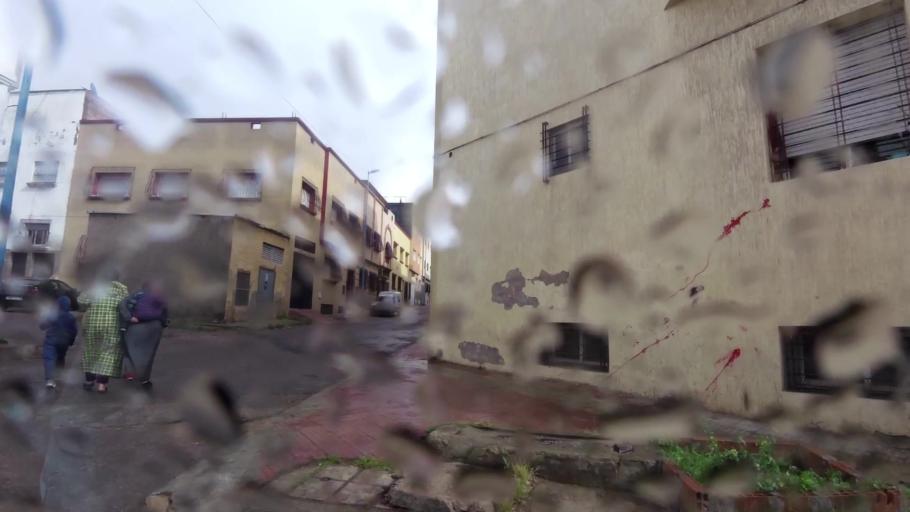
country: MA
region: Grand Casablanca
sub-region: Casablanca
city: Casablanca
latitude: 33.5647
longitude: -7.6935
